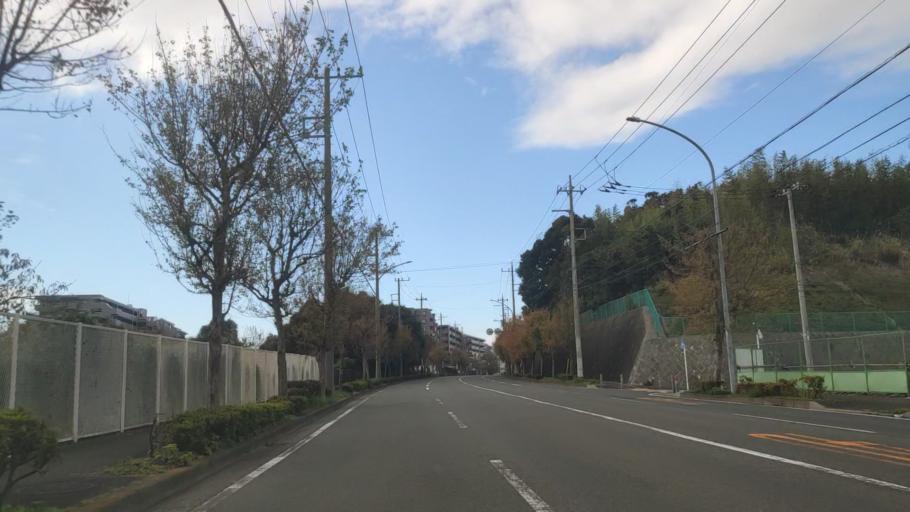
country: JP
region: Kanagawa
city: Minami-rinkan
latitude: 35.4275
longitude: 139.5147
